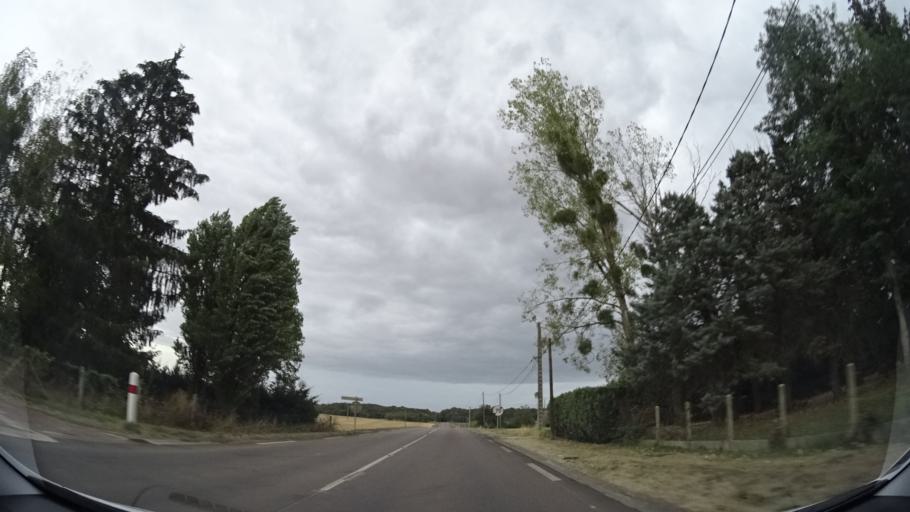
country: FR
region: Bourgogne
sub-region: Departement de l'Yonne
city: Charny
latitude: 47.9366
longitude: 3.1550
